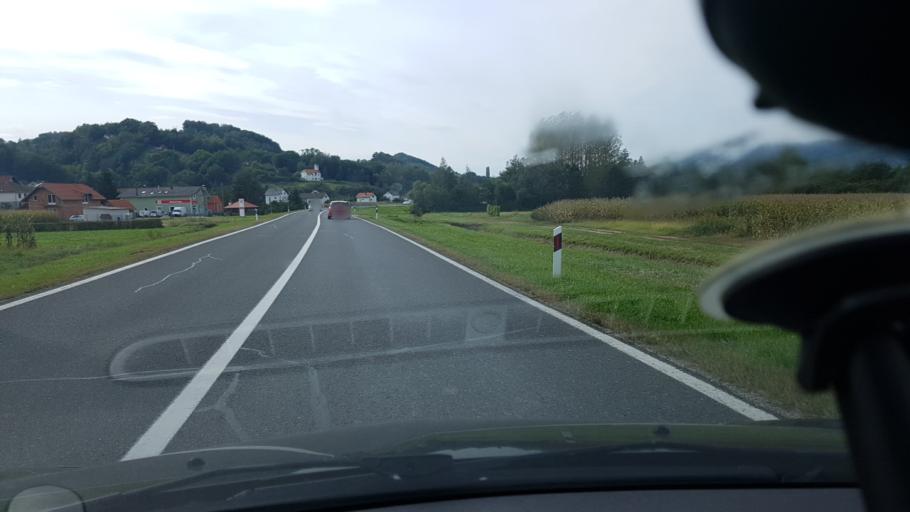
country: HR
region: Varazdinska
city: Ljubescica
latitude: 46.1498
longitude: 16.3611
